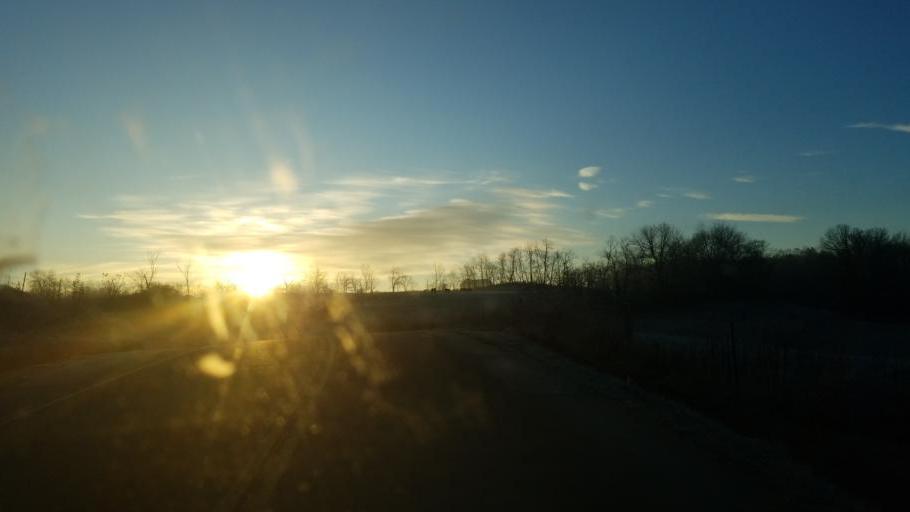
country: US
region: Ohio
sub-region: Holmes County
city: Millersburg
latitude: 40.6258
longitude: -81.8385
